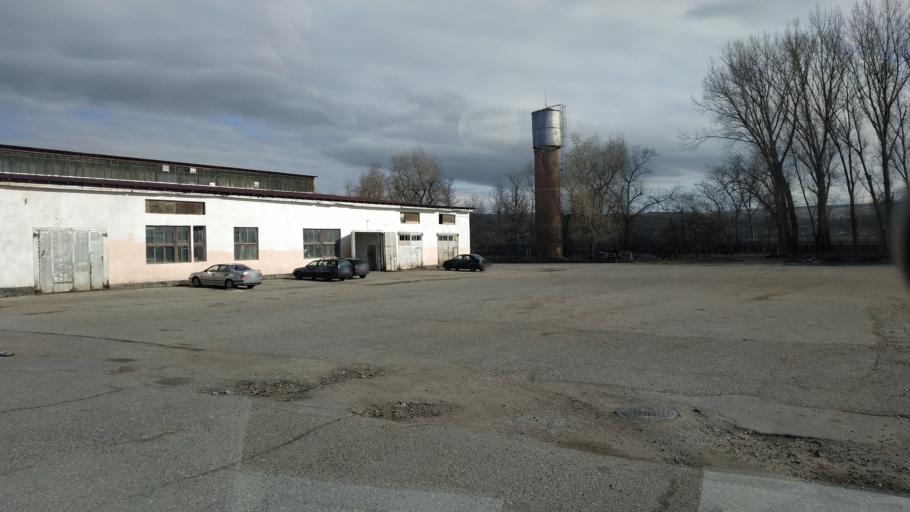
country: MD
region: Causeni
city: Causeni
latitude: 46.6588
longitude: 29.4215
